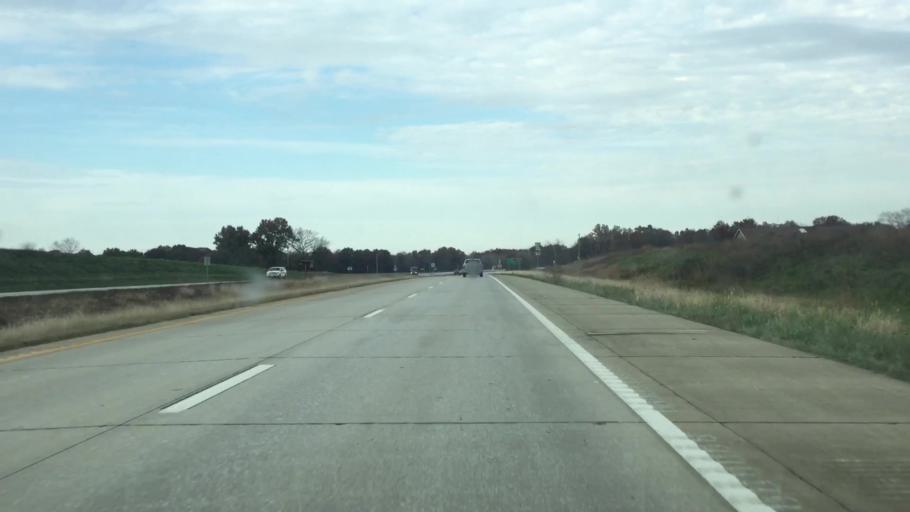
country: US
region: Missouri
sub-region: Henry County
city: Clinton
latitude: 38.3490
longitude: -93.7566
